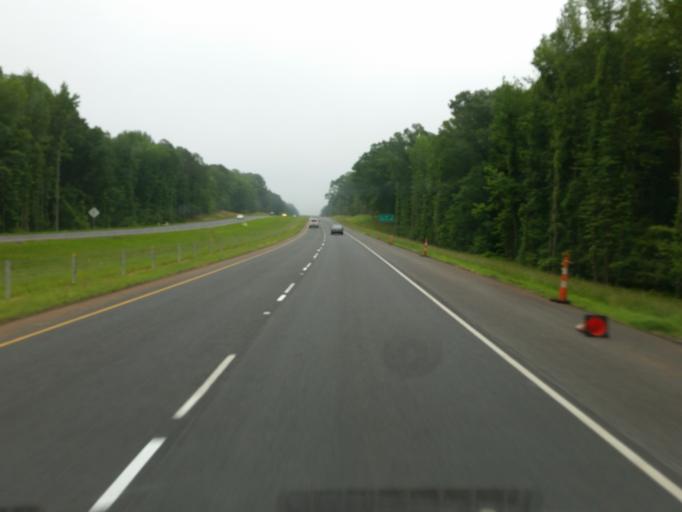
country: US
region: Louisiana
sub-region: Webster Parish
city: Minden
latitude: 32.5616
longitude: -93.1477
